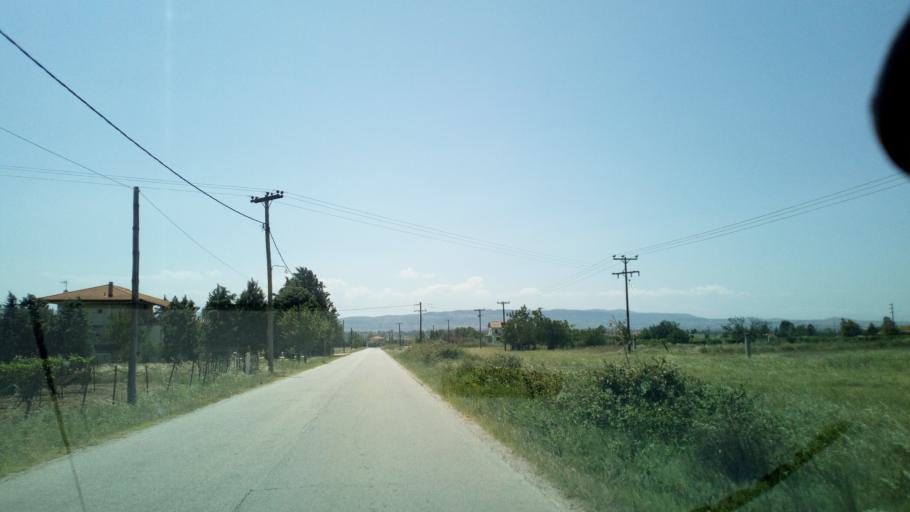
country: GR
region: Central Macedonia
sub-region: Nomos Thessalonikis
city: Lagkadas
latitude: 40.7695
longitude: 23.0902
